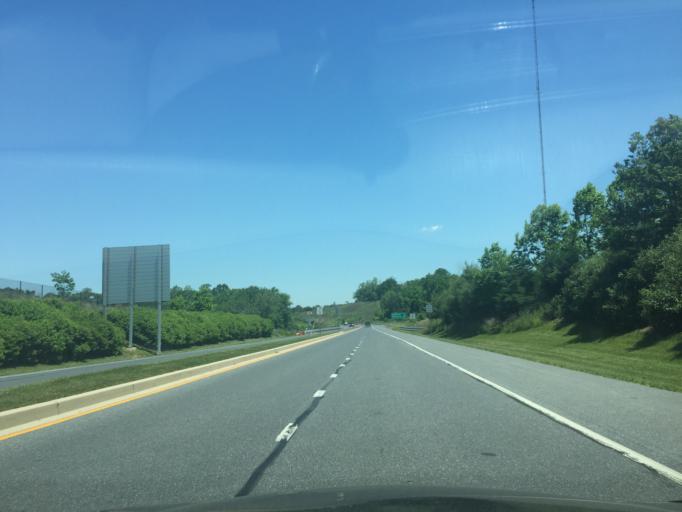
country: US
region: Maryland
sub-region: Carroll County
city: Hampstead
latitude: 39.6131
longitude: -76.8634
